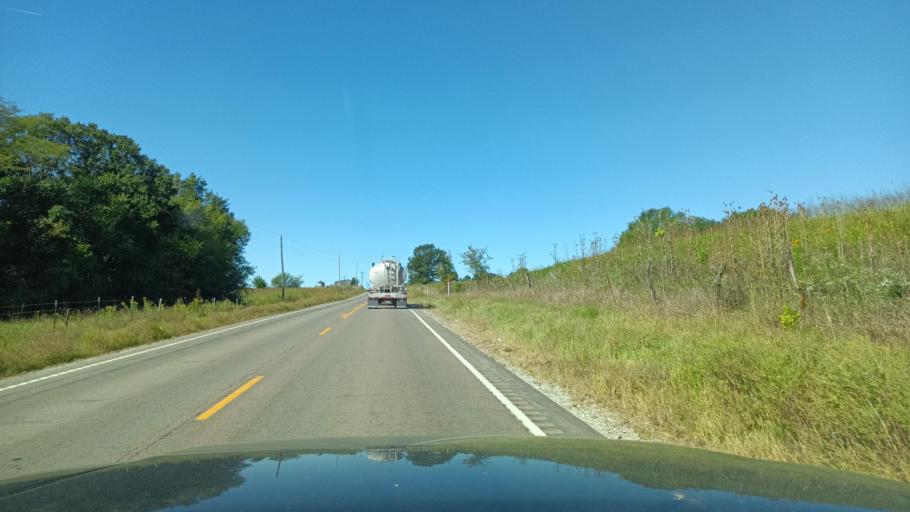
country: US
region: Missouri
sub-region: Scotland County
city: Memphis
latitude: 40.4559
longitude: -92.1209
